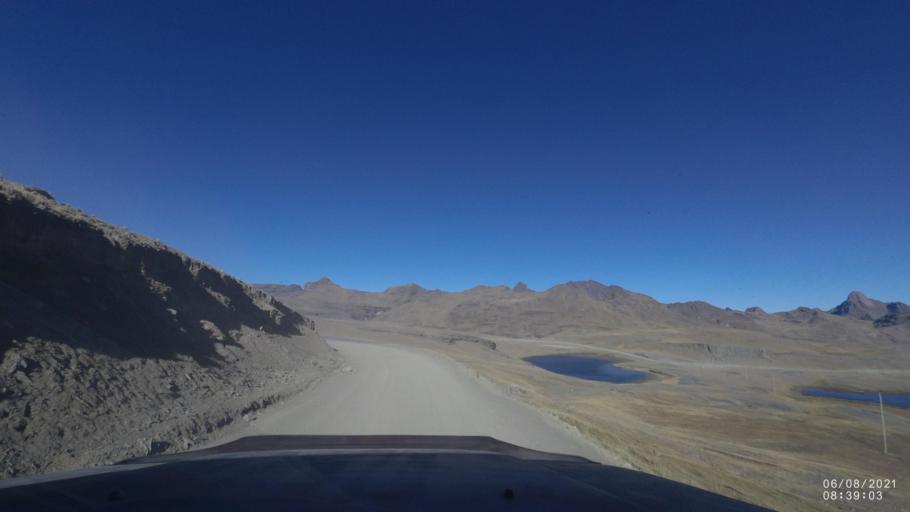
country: BO
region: Cochabamba
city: Sipe Sipe
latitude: -17.1730
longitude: -66.3963
